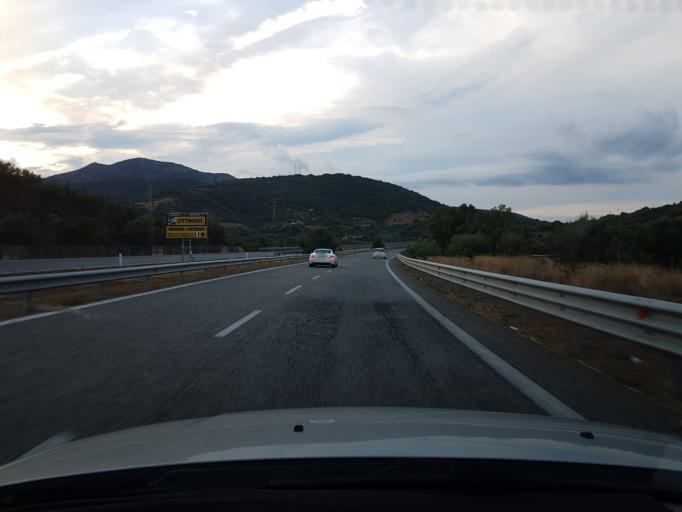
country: IT
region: Sardinia
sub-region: Provincia di Olbia-Tempio
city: San Teodoro
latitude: 40.7283
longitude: 9.6525
